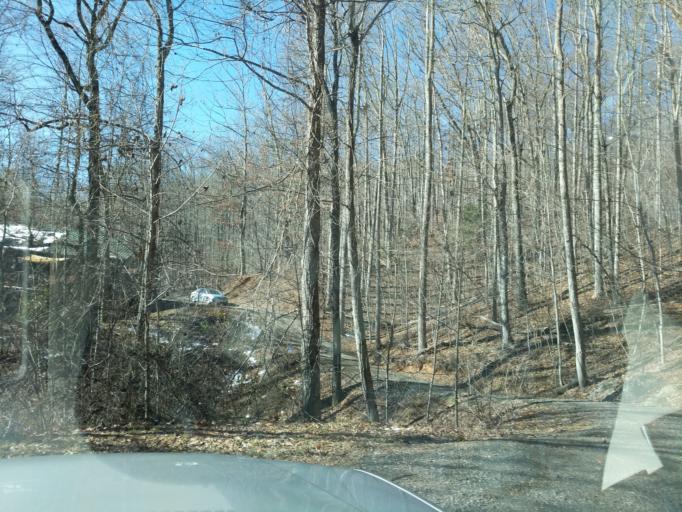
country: US
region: Georgia
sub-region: Towns County
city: Hiawassee
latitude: 34.9498
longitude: -83.7310
